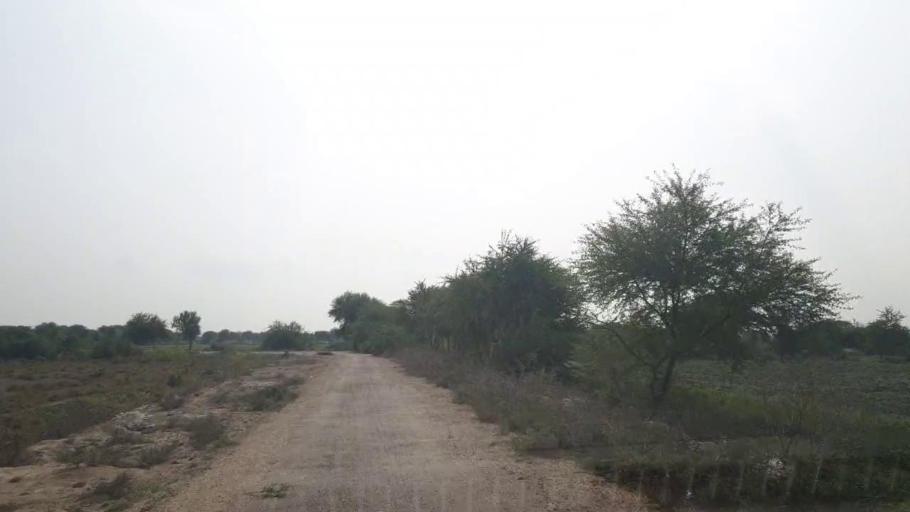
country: PK
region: Sindh
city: Badin
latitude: 24.5483
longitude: 68.6877
